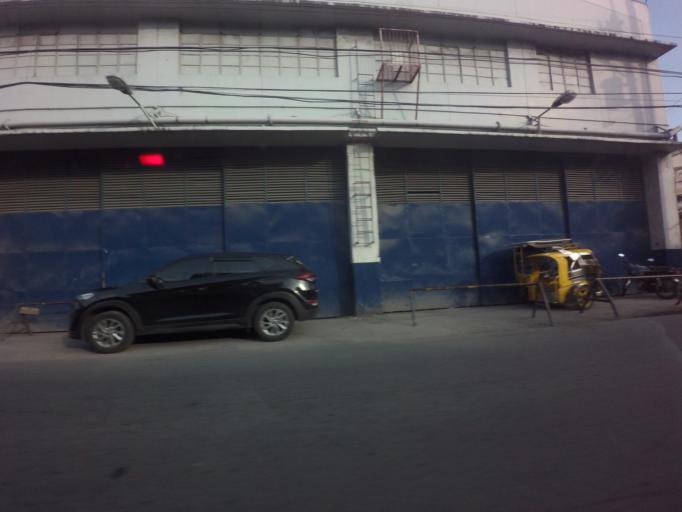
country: PH
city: Sambayanihan People's Village
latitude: 14.4977
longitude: 121.0044
